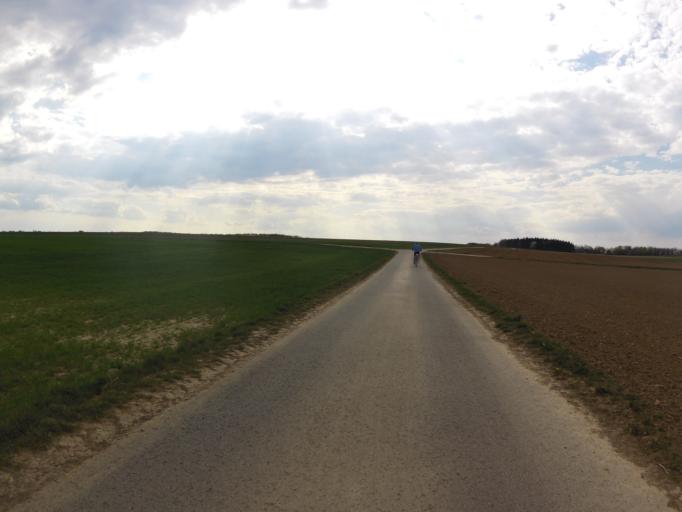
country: DE
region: Bavaria
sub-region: Regierungsbezirk Unterfranken
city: Oberpleichfeld
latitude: 49.8415
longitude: 10.0841
